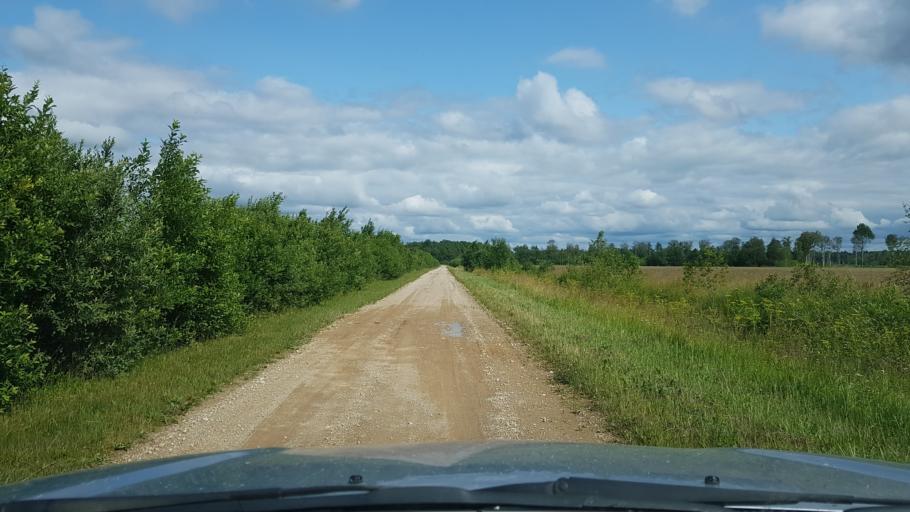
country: EE
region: Ida-Virumaa
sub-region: Narva-Joesuu linn
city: Narva-Joesuu
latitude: 59.3703
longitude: 27.9157
